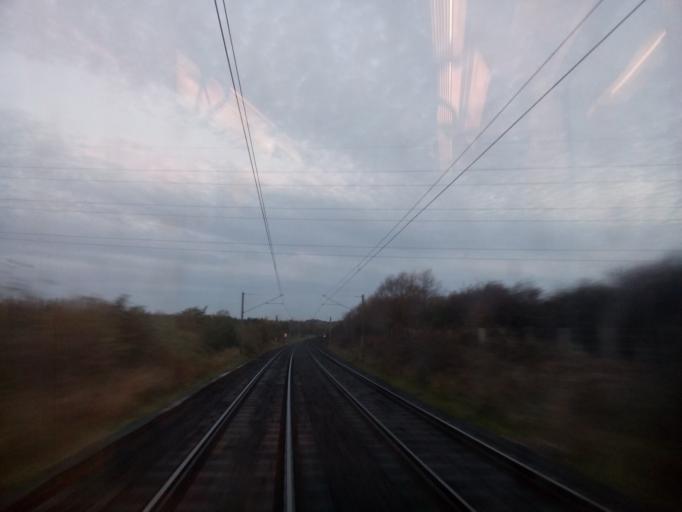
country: GB
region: England
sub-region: Newcastle upon Tyne
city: Dinnington
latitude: 55.0168
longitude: -1.6874
